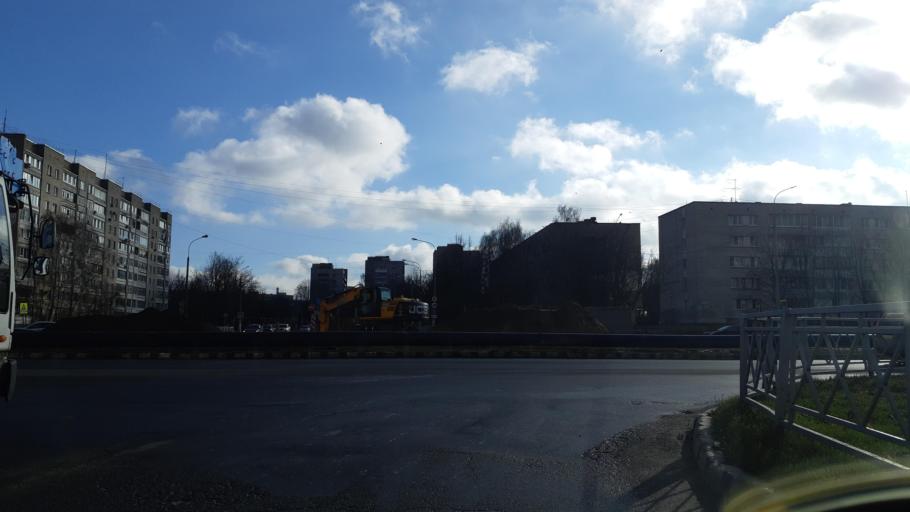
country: RU
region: Kaluga
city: Obninsk
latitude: 55.1212
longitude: 36.6044
